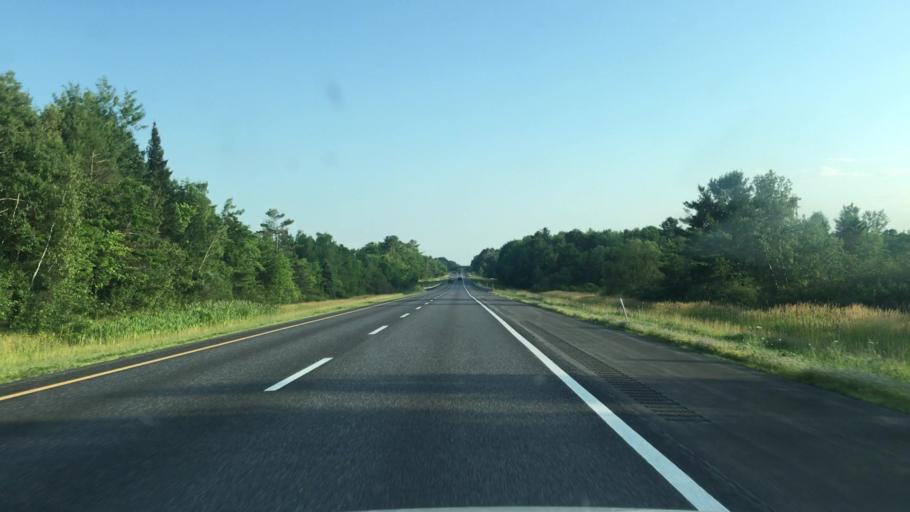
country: US
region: Maine
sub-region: Sagadahoc County
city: Richmond
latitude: 44.1404
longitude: -69.8433
